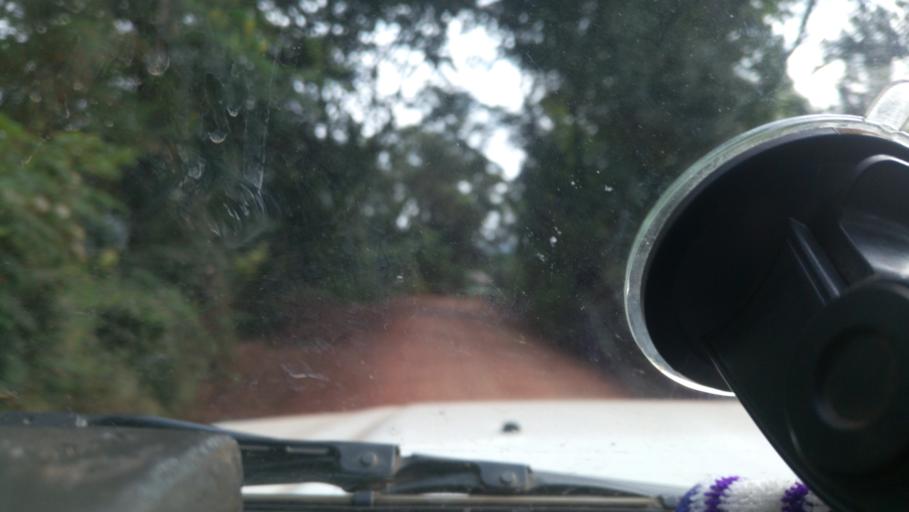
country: KE
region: Kericho
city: Litein
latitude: -0.5509
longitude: 35.2002
